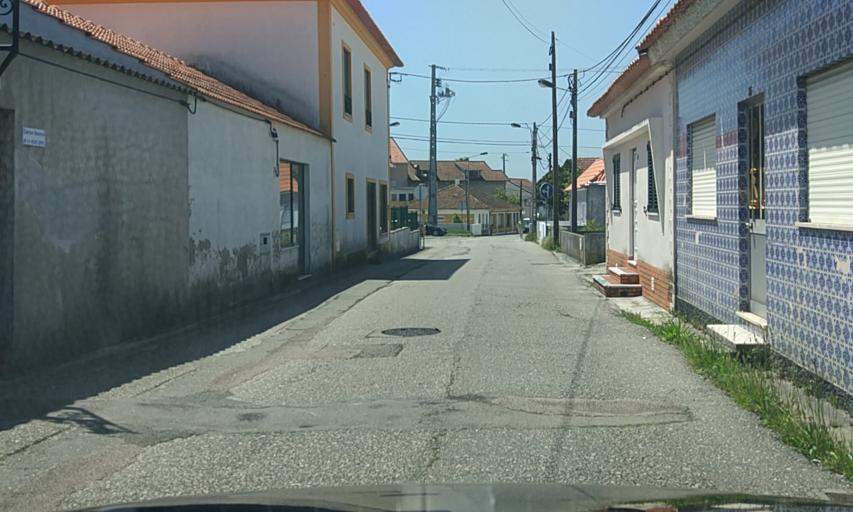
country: PT
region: Aveiro
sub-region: Aveiro
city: Aveiro
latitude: 40.6433
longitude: -8.6197
